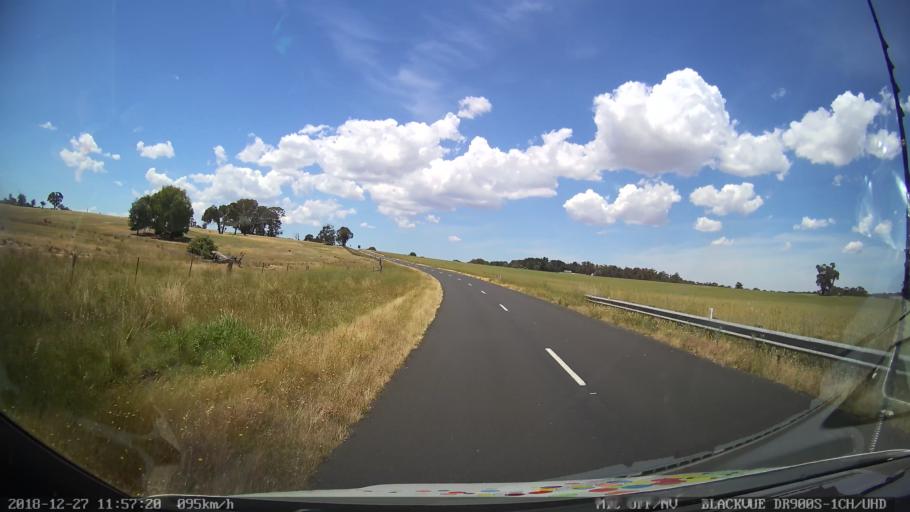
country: AU
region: New South Wales
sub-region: Blayney
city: Blayney
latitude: -33.7102
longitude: 149.3864
